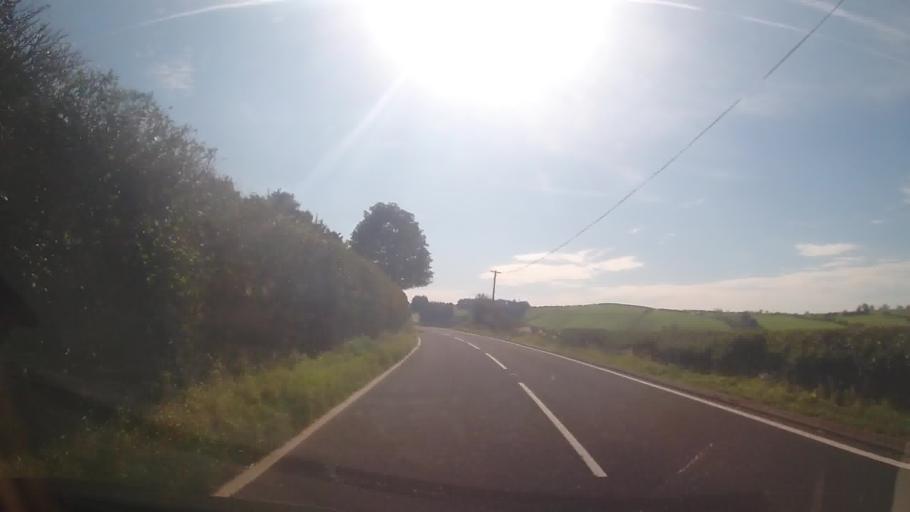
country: GB
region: Wales
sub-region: Sir Powys
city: Mochdre
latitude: 52.4586
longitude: -3.3473
